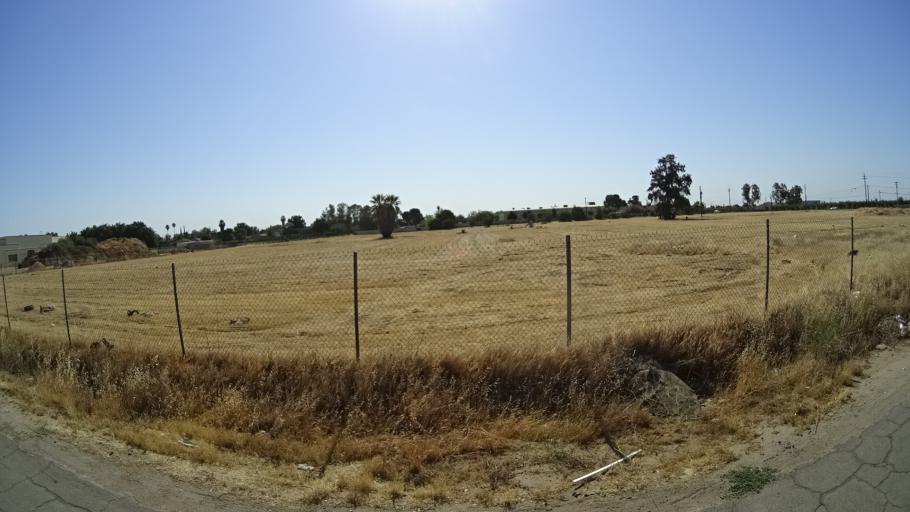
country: US
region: California
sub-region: Fresno County
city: West Park
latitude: 36.7228
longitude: -119.8312
